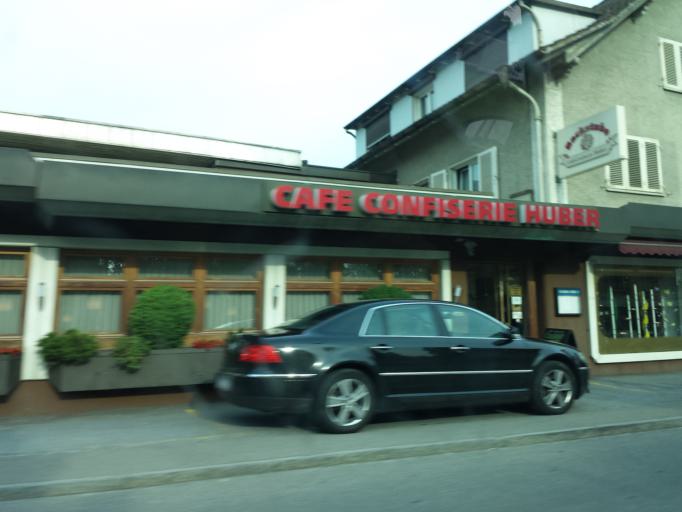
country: CH
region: Appenzell Innerrhoden
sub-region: Appenzell Inner Rhodes
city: Balgach
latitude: 47.4047
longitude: 9.6349
